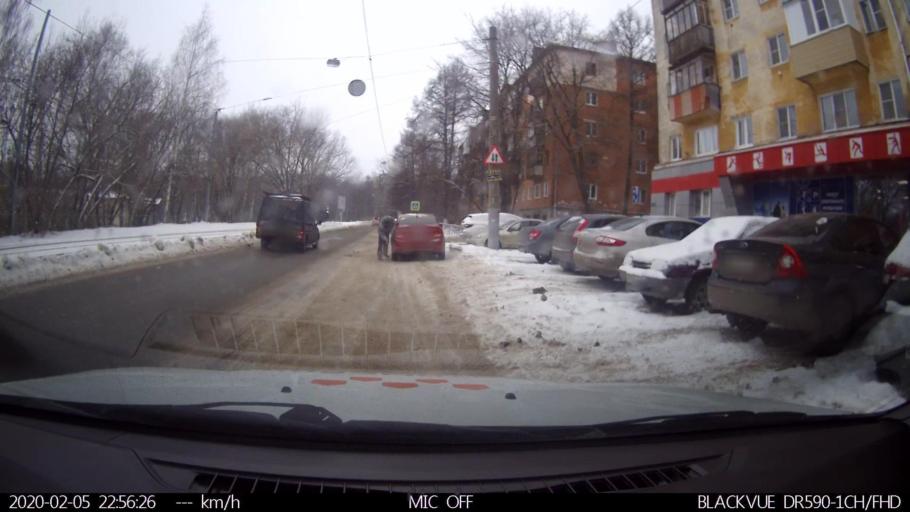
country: RU
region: Penza
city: Bogoslovka
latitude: 53.2954
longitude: 44.8281
